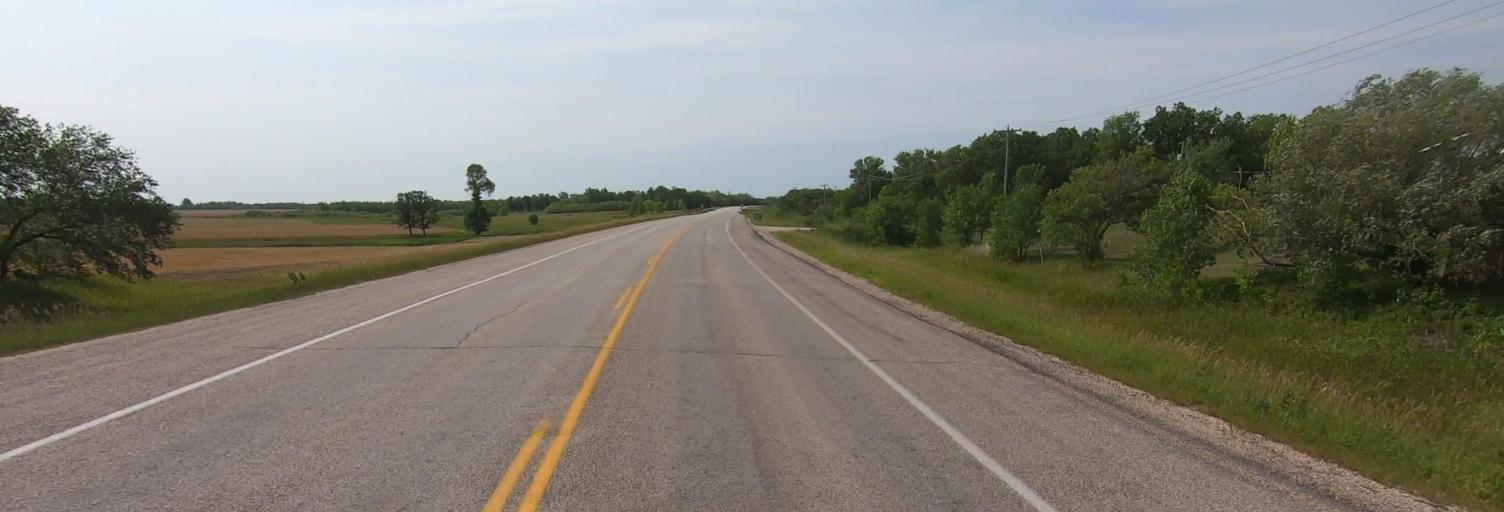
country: CA
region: Manitoba
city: Niverville
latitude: 49.6368
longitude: -97.1068
